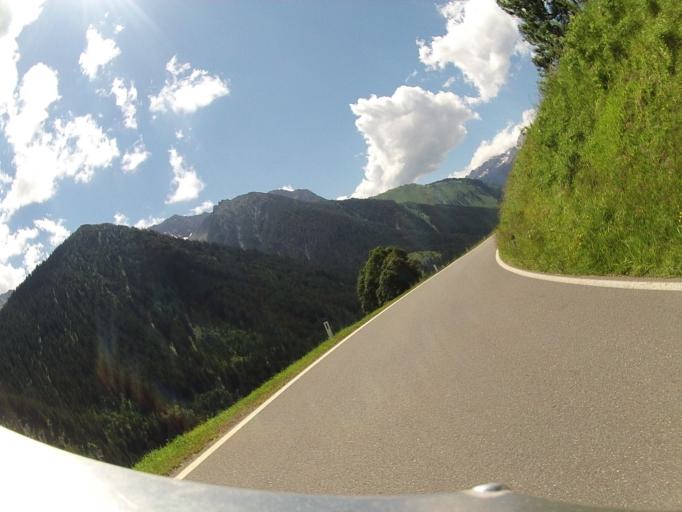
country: AT
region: Tyrol
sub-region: Politischer Bezirk Reutte
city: Elmen
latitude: 47.3102
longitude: 10.5823
